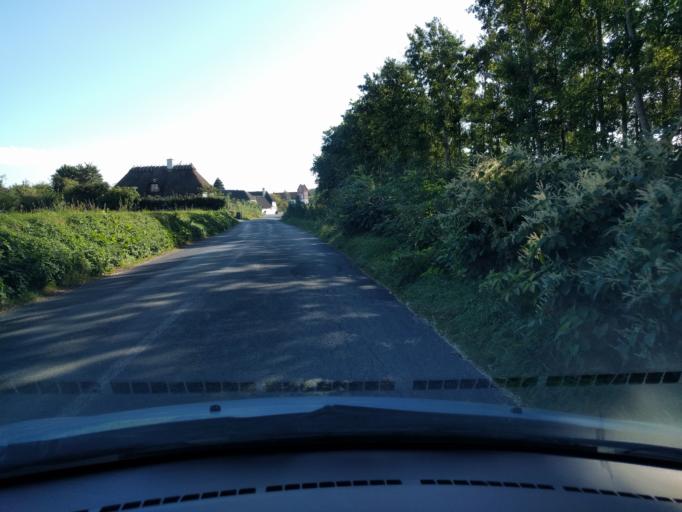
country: DK
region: South Denmark
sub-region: Assens Kommune
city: Harby
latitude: 55.1450
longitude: 10.0199
